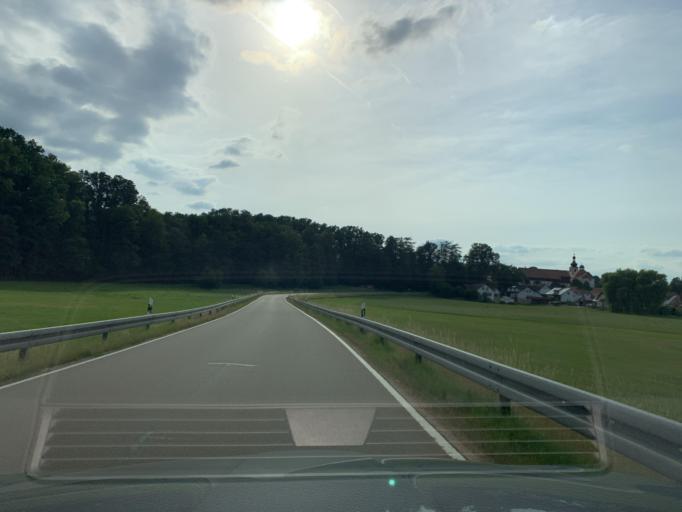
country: DE
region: Bavaria
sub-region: Upper Palatinate
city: Pettendorf
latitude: 49.3493
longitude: 12.3672
